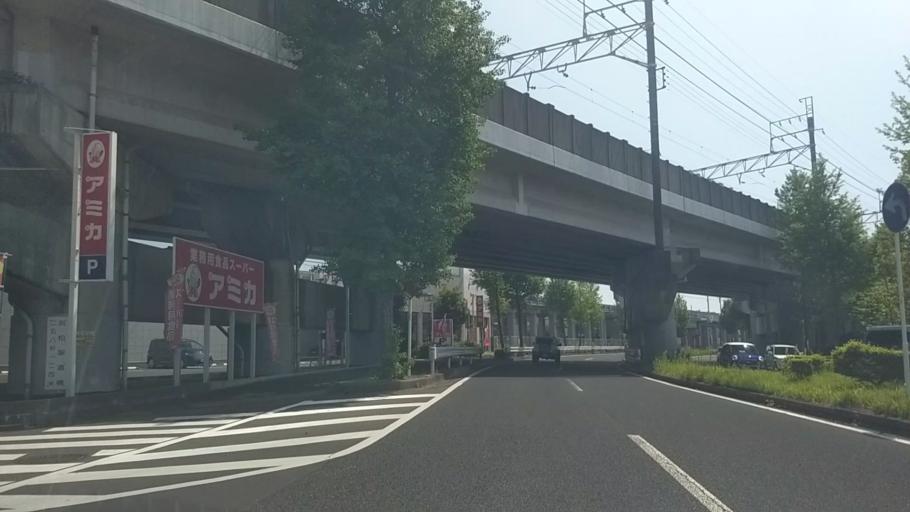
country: JP
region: Shizuoka
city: Hamamatsu
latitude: 34.6986
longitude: 137.7265
